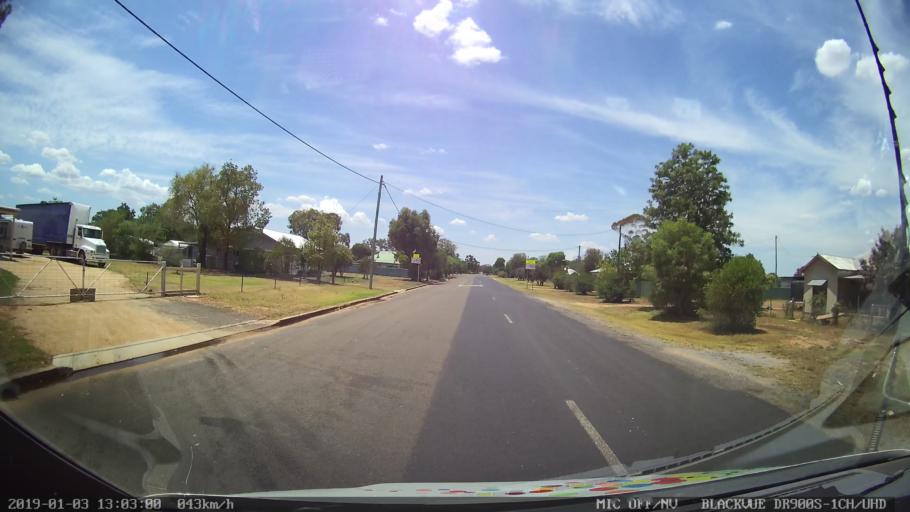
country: AU
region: New South Wales
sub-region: Cabonne
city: Canowindra
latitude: -33.6173
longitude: 148.4333
